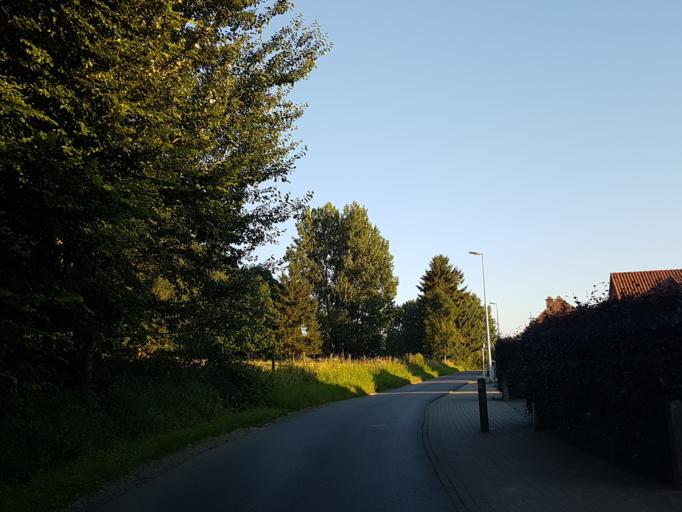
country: BE
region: Flanders
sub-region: Provincie Vlaams-Brabant
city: Dilbeek
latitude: 50.8735
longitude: 4.2292
